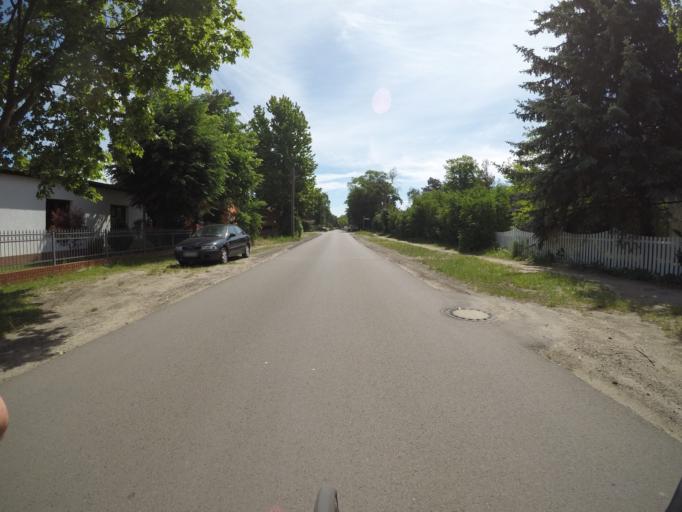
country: DE
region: Berlin
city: Mahlsdorf
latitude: 52.4934
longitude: 13.6152
